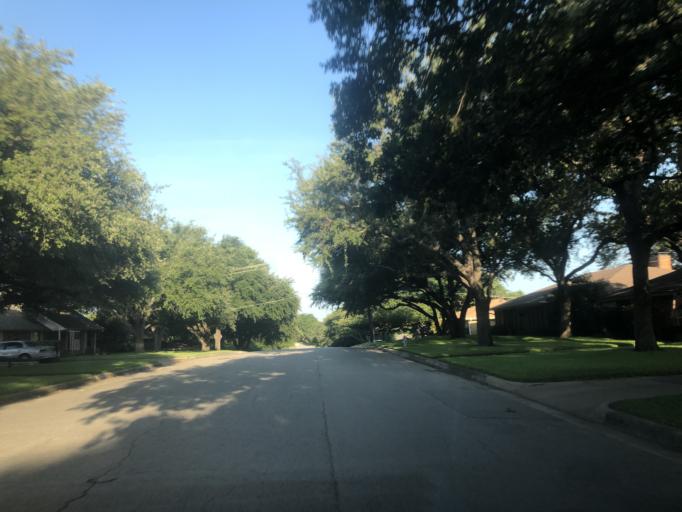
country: US
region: Texas
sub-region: Tarrant County
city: Edgecliff Village
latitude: 32.6558
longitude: -97.3932
